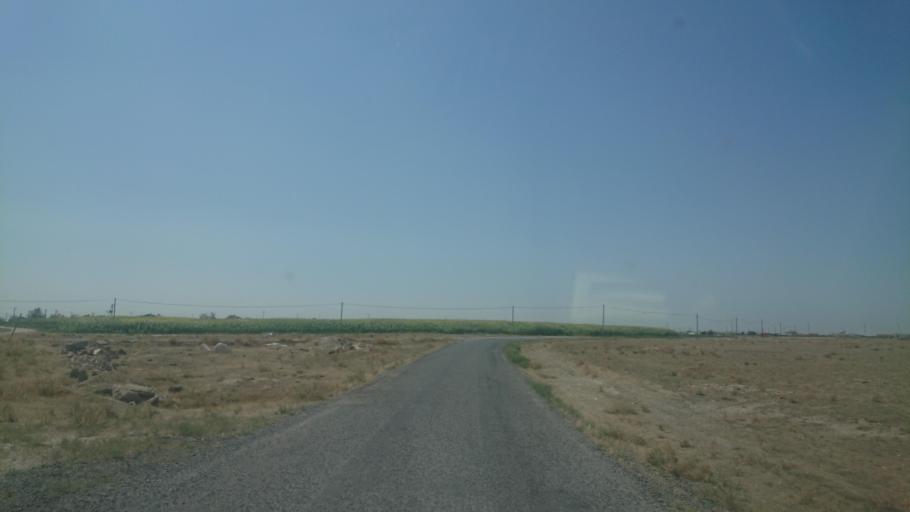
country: TR
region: Aksaray
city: Yesilova
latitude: 38.2963
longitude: 33.7282
